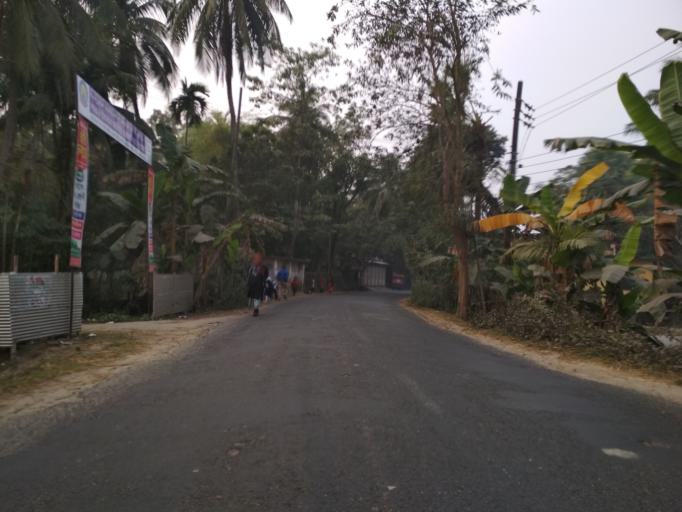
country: BD
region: Chittagong
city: Lakshmipur
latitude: 22.9236
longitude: 90.8347
